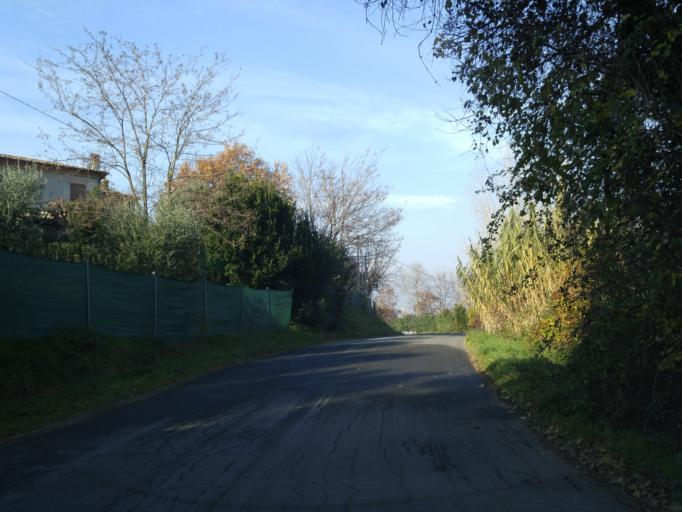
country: IT
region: The Marches
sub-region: Provincia di Pesaro e Urbino
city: Tavernelle
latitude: 43.7147
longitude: 12.9112
